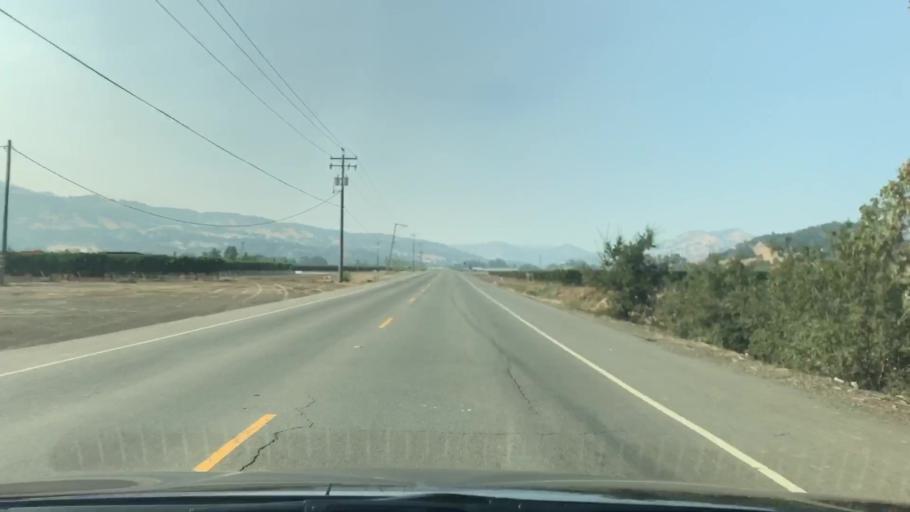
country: US
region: California
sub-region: Solano County
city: Green Valley
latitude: 38.2815
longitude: -122.1165
